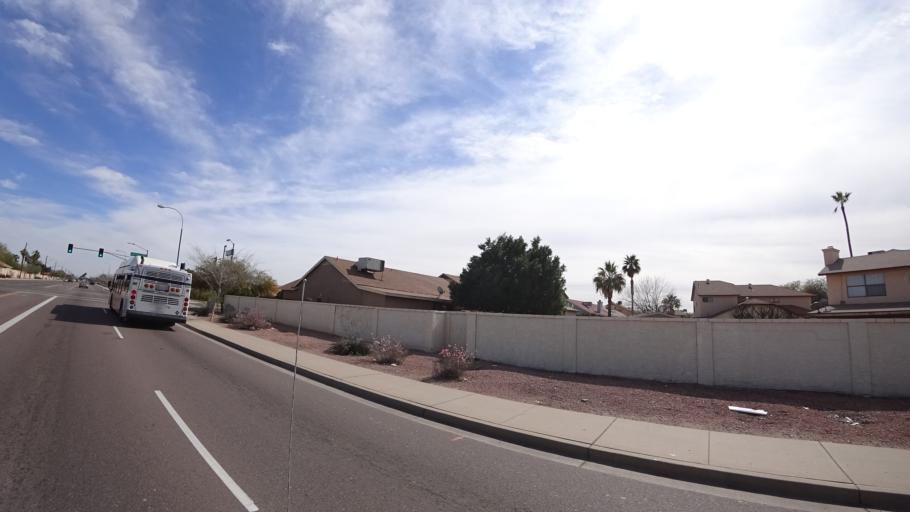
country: US
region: Arizona
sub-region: Maricopa County
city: Tolleson
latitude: 33.4796
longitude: -112.2472
